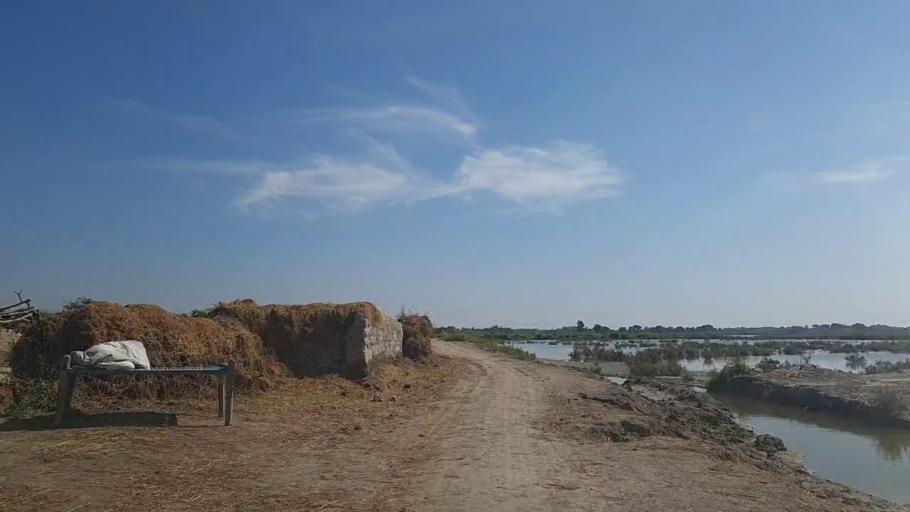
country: PK
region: Sindh
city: Mirpur Batoro
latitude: 24.7540
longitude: 68.3057
